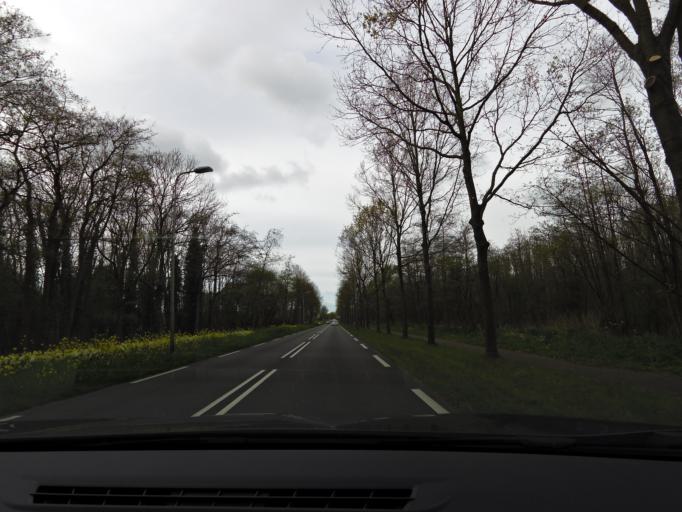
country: NL
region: South Holland
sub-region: Gemeente Lisse
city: Lisse
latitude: 52.2731
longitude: 4.5389
